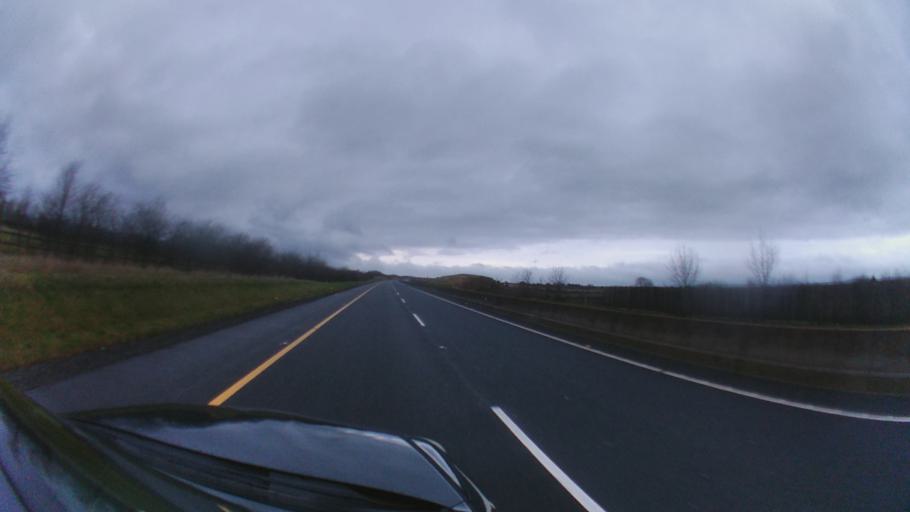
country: IE
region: Leinster
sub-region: County Carlow
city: Bagenalstown
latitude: 52.7480
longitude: -6.9936
